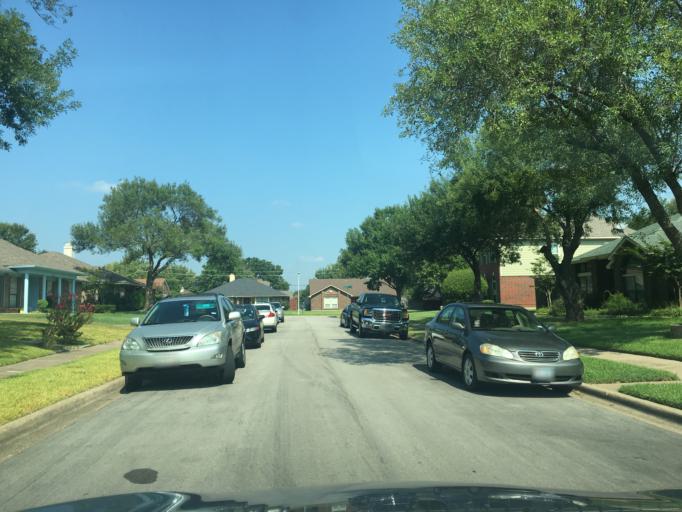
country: US
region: Texas
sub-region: Dallas County
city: Garland
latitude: 32.9448
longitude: -96.6277
